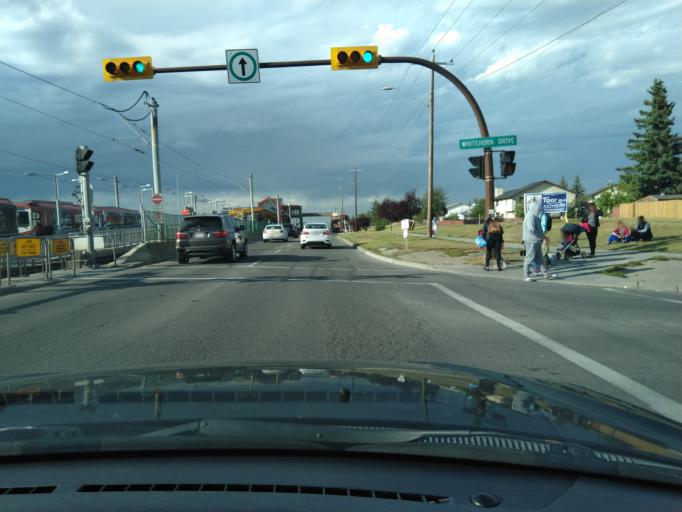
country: CA
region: Alberta
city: Calgary
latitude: 51.0849
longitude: -113.9815
